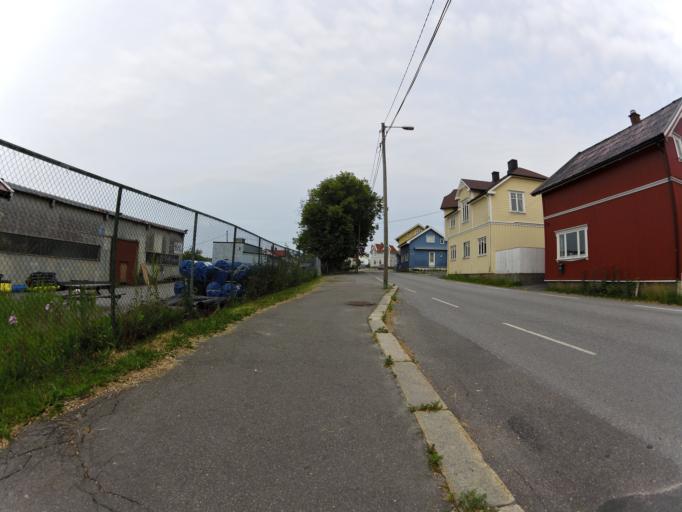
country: NO
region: Ostfold
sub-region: Fredrikstad
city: Fredrikstad
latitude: 59.2128
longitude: 10.9660
